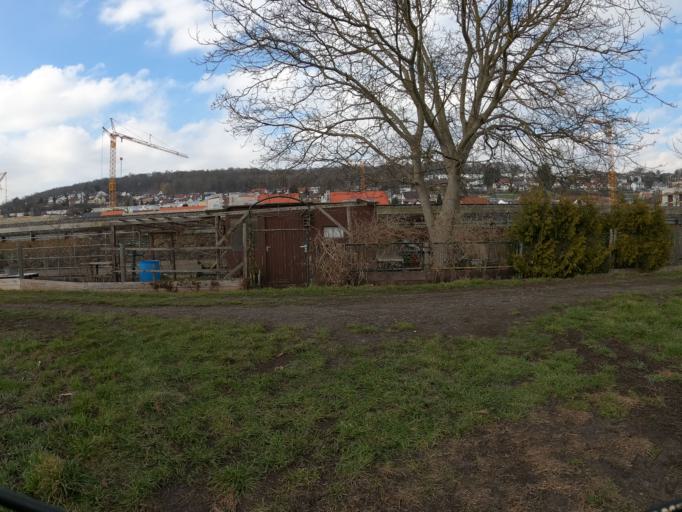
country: DE
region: Bavaria
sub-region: Swabia
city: Nersingen
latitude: 48.4462
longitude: 10.0782
